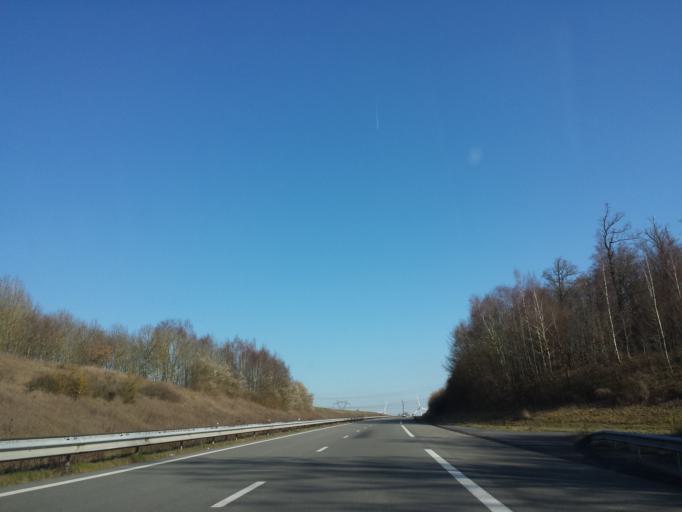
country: FR
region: Picardie
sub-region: Departement de la Somme
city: Conty
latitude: 49.6801
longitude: 2.2153
